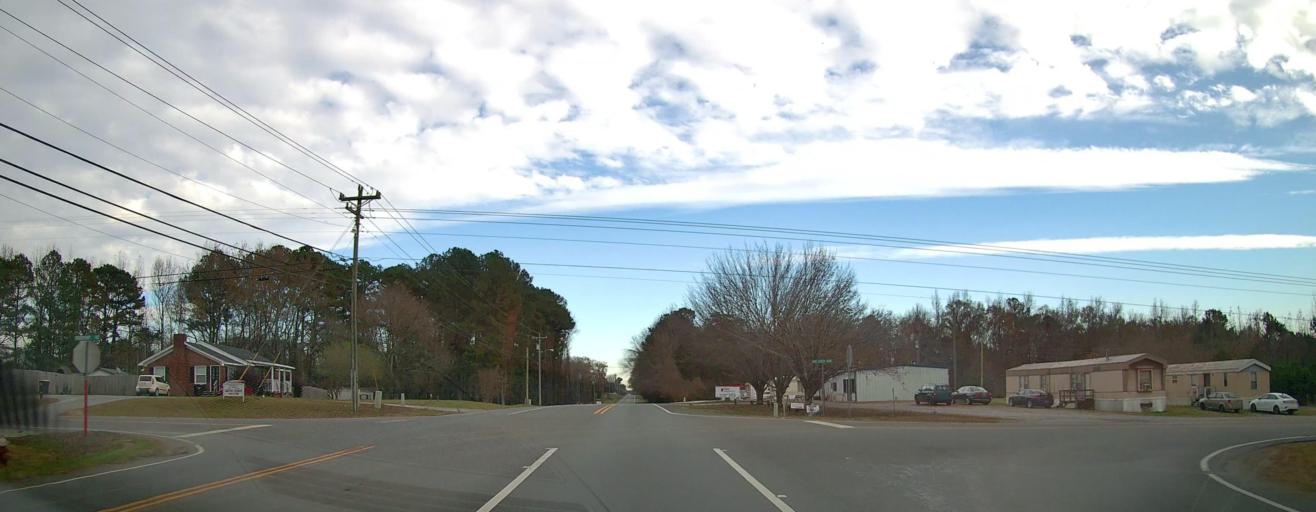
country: US
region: Alabama
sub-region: Morgan County
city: Priceville
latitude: 34.5010
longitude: -86.8553
